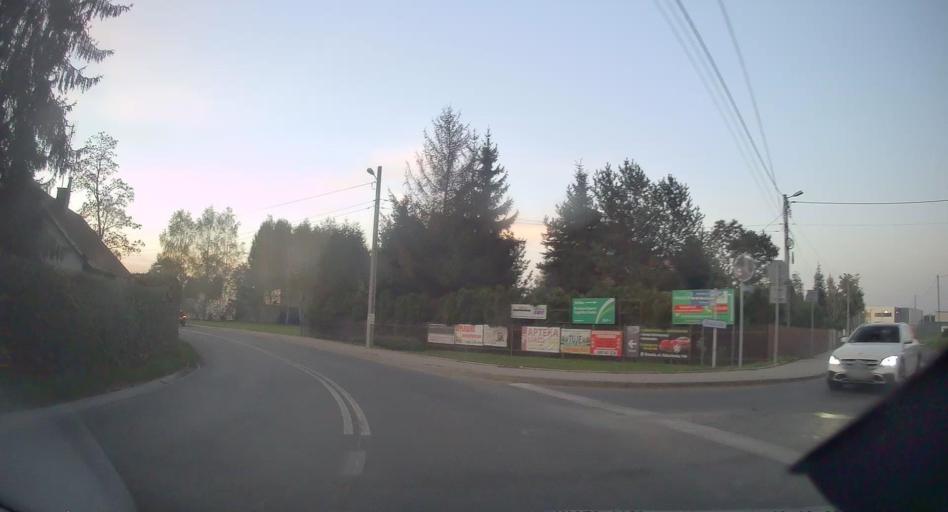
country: PL
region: Lesser Poland Voivodeship
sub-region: Powiat krakowski
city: Rzaska
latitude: 50.1106
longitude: 19.8406
